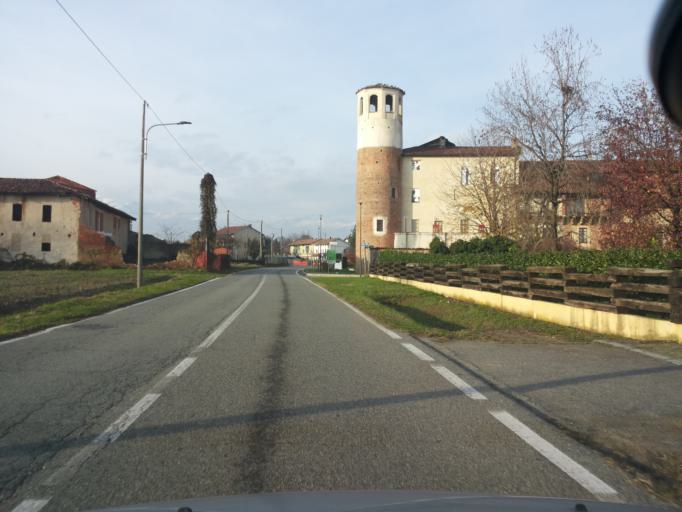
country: IT
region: Piedmont
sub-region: Provincia di Biella
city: Verrone
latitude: 45.5015
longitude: 8.1170
